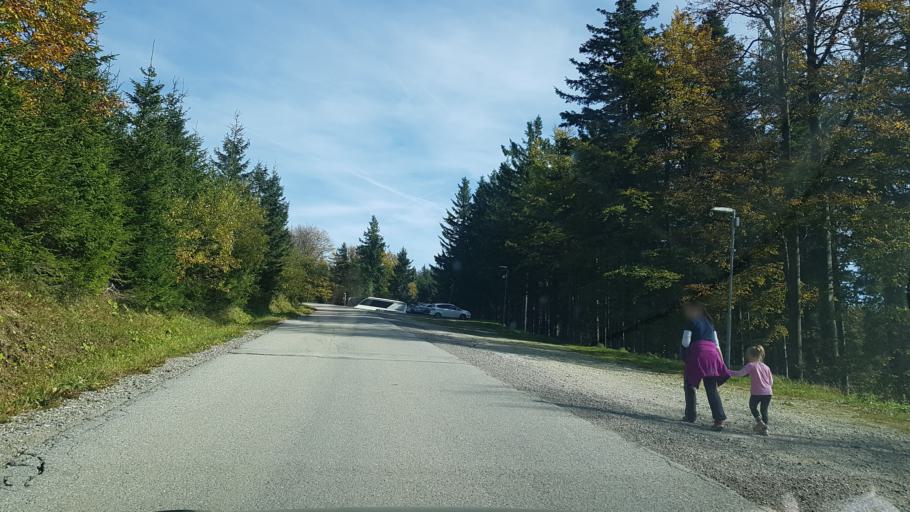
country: SI
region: Mislinja
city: Mislinja
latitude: 46.5019
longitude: 15.2086
